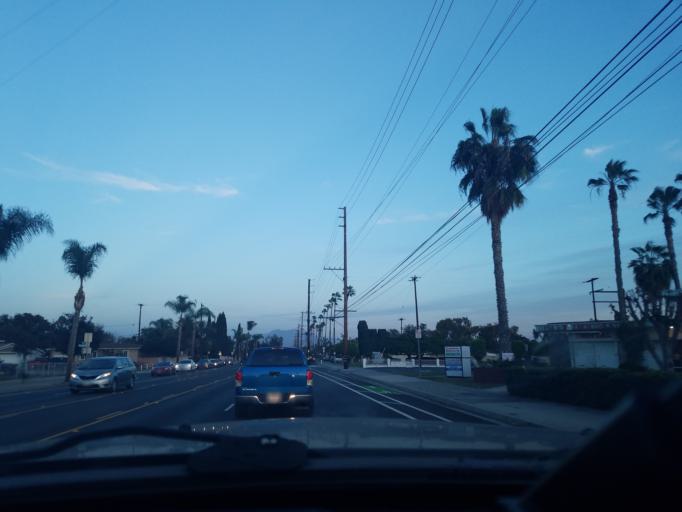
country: US
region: California
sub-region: Orange County
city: Santa Ana
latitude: 33.7161
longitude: -117.8833
